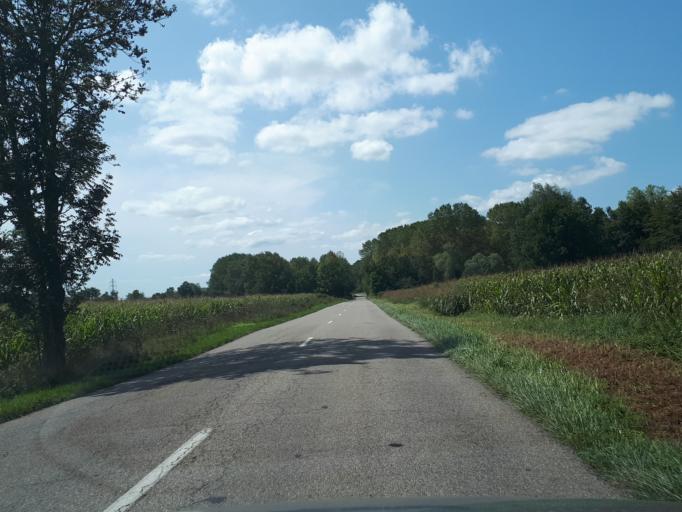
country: FR
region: Rhone-Alpes
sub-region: Departement de l'Isere
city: L'Isle-d'Abeau
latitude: 45.6353
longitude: 5.2299
